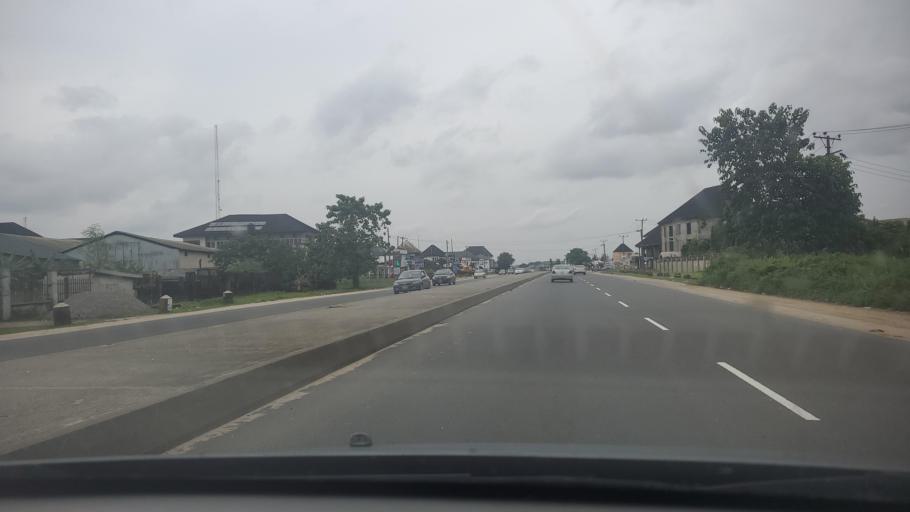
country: NG
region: Rivers
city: Emuoha
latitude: 4.8736
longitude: 6.9592
